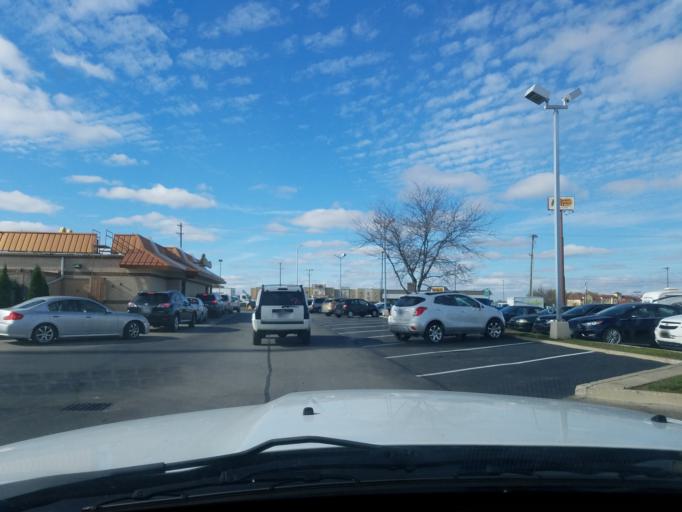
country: US
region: Indiana
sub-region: Montgomery County
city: Crawfordsville
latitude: 40.0764
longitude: -86.9039
